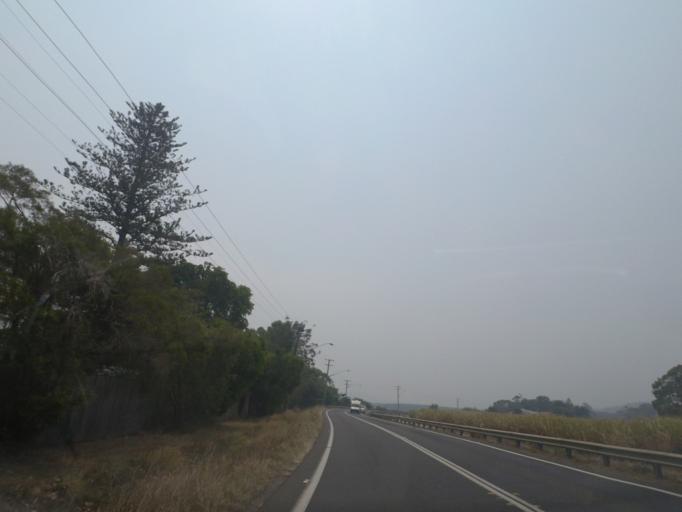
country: AU
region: New South Wales
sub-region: Richmond Valley
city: Evans Head
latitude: -29.0068
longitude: 153.4366
